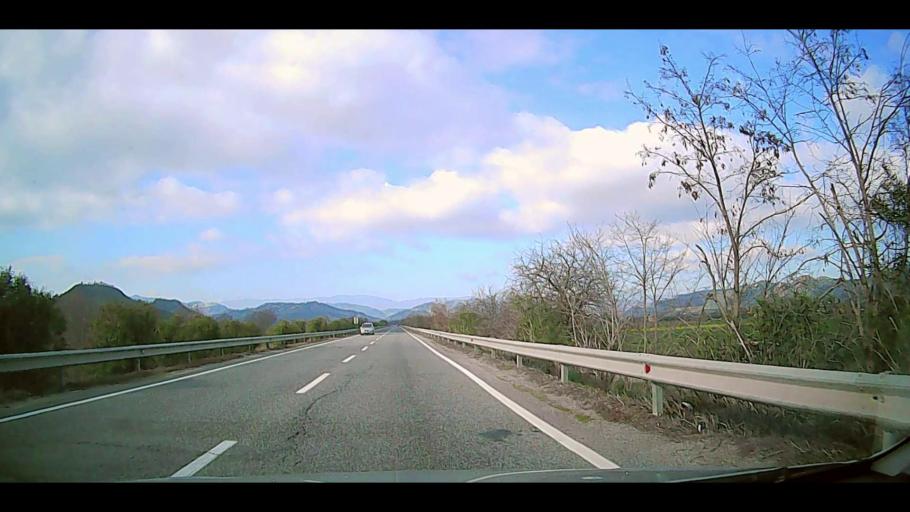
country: IT
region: Calabria
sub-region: Provincia di Crotone
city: Rocca di Neto
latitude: 39.1692
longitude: 16.9748
